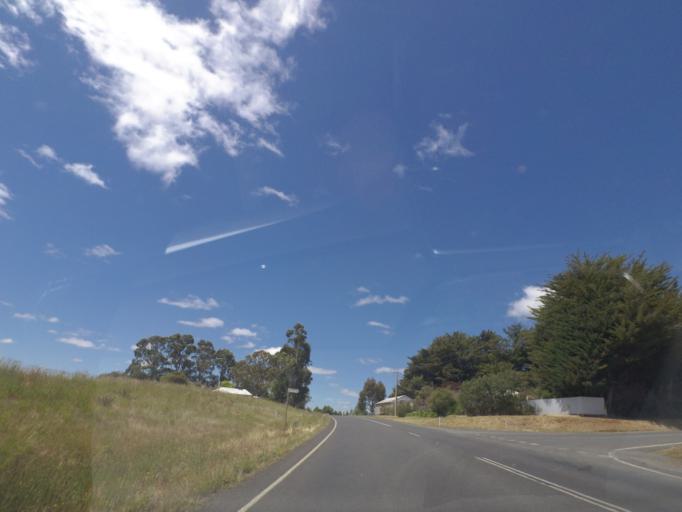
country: AU
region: Victoria
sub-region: Mount Alexander
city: Castlemaine
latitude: -37.3303
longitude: 144.1860
